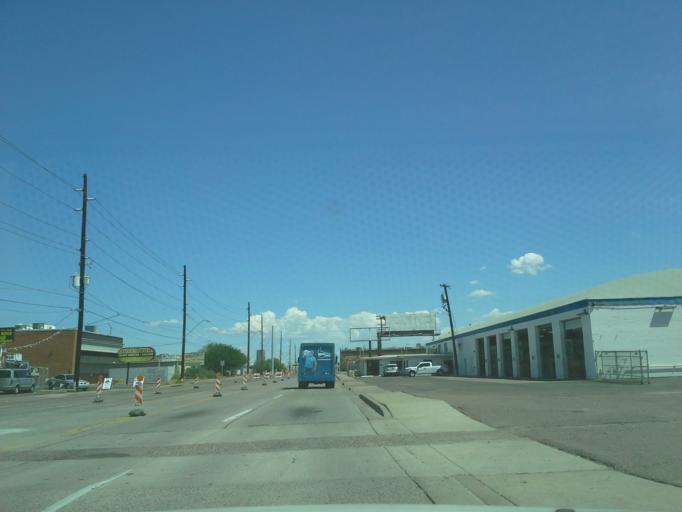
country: US
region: Arizona
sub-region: Maricopa County
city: Phoenix
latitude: 33.4658
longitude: -112.1076
